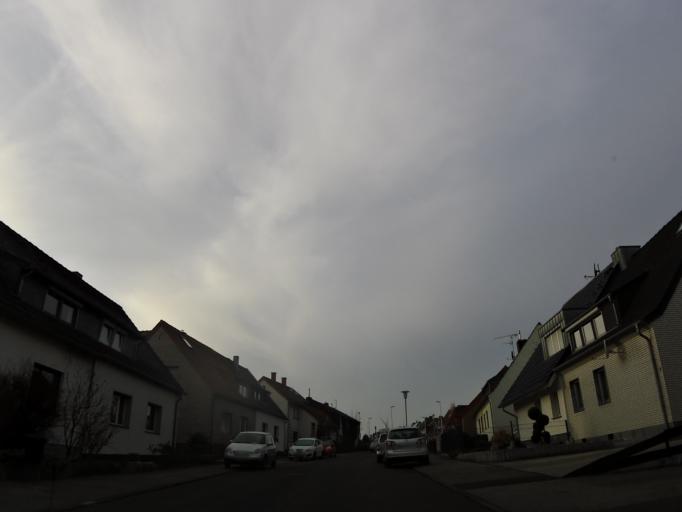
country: DE
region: North Rhine-Westphalia
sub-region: Regierungsbezirk Koln
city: Herzogenrath
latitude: 50.8396
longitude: 6.0922
